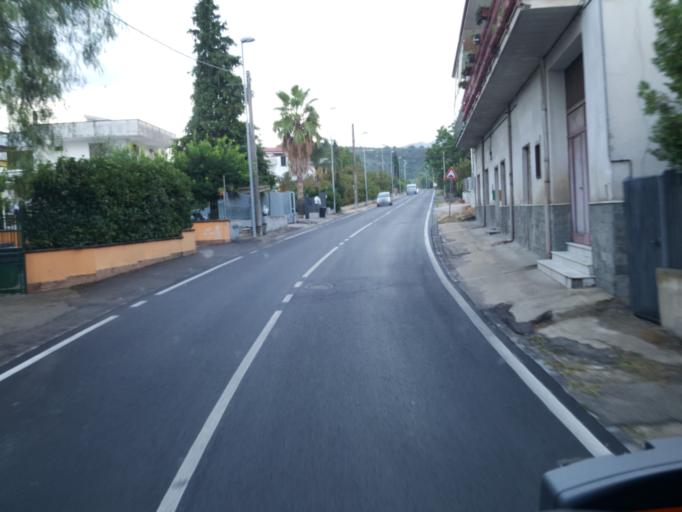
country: IT
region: Campania
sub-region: Provincia di Napoli
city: Carbonara di Nola
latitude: 40.8807
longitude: 14.5671
